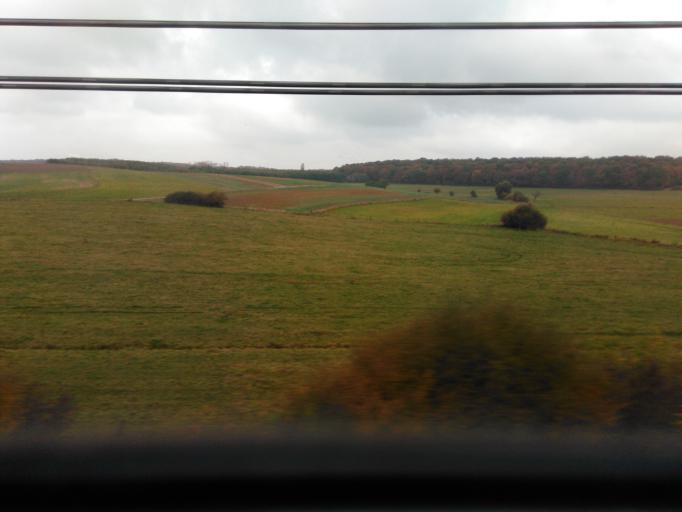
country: LU
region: Luxembourg
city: Fentange
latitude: 49.5578
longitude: 6.1443
